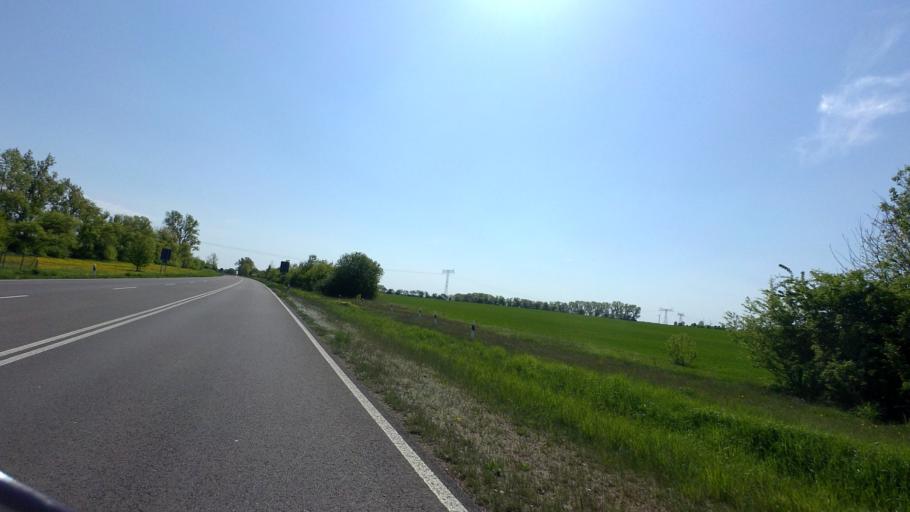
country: DE
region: Brandenburg
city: Beeskow
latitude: 52.1841
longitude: 14.2174
